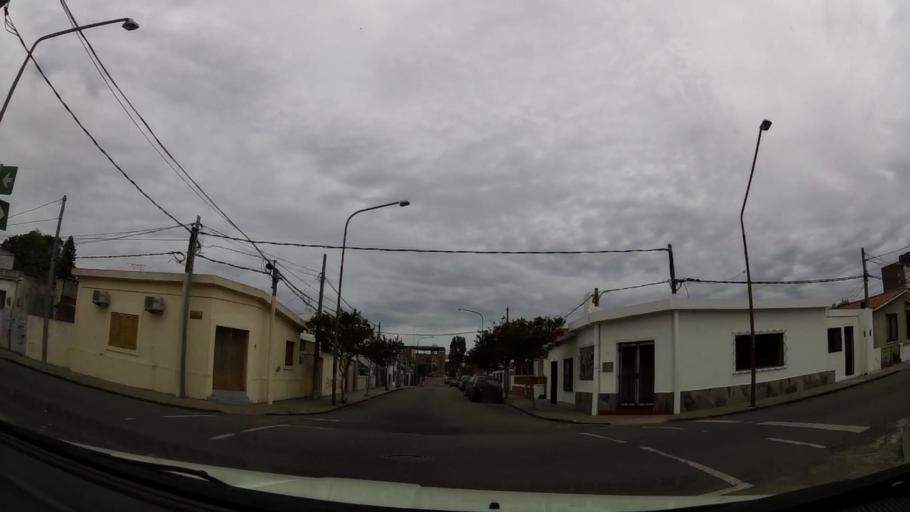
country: UY
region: Maldonado
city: Maldonado
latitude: -34.9107
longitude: -54.9555
